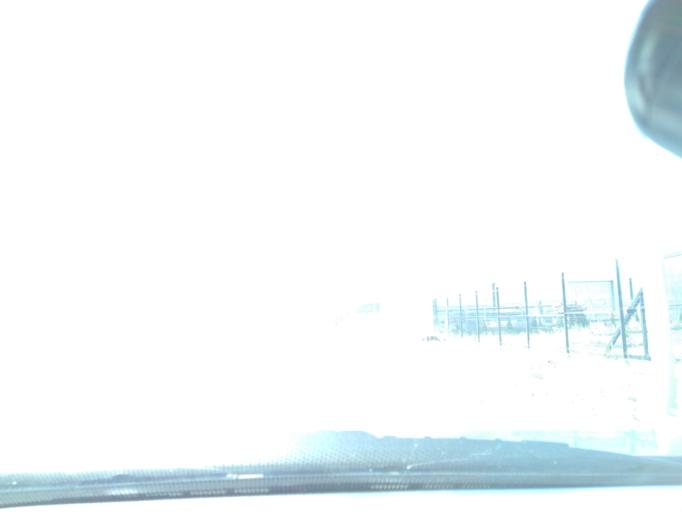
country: PL
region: Silesian Voivodeship
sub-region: Gliwice
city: Gliwice
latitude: 50.2787
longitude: 18.6874
